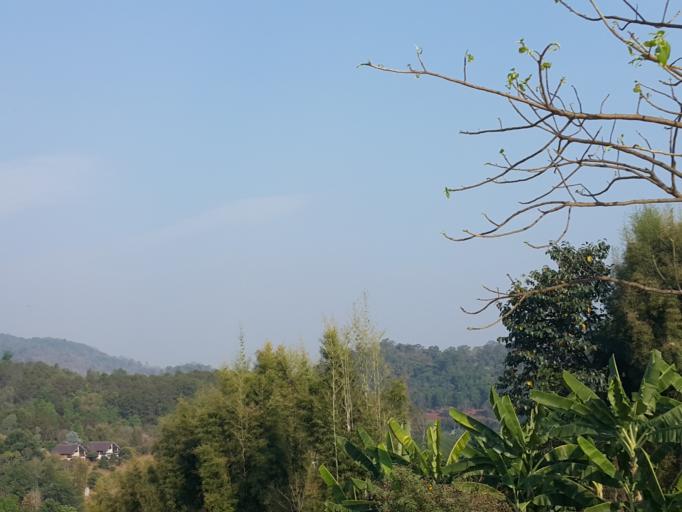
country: TH
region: Chiang Mai
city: Samoeng
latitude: 18.9113
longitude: 98.8026
